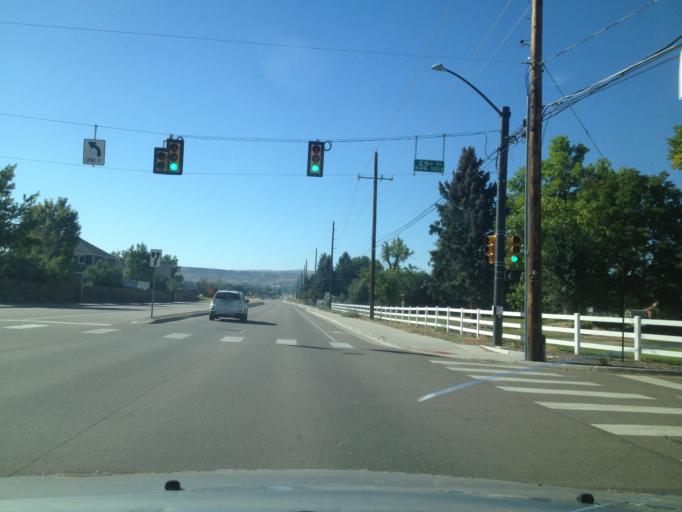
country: US
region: Colorado
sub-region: Jefferson County
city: Applewood
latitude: 39.7909
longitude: -105.1746
